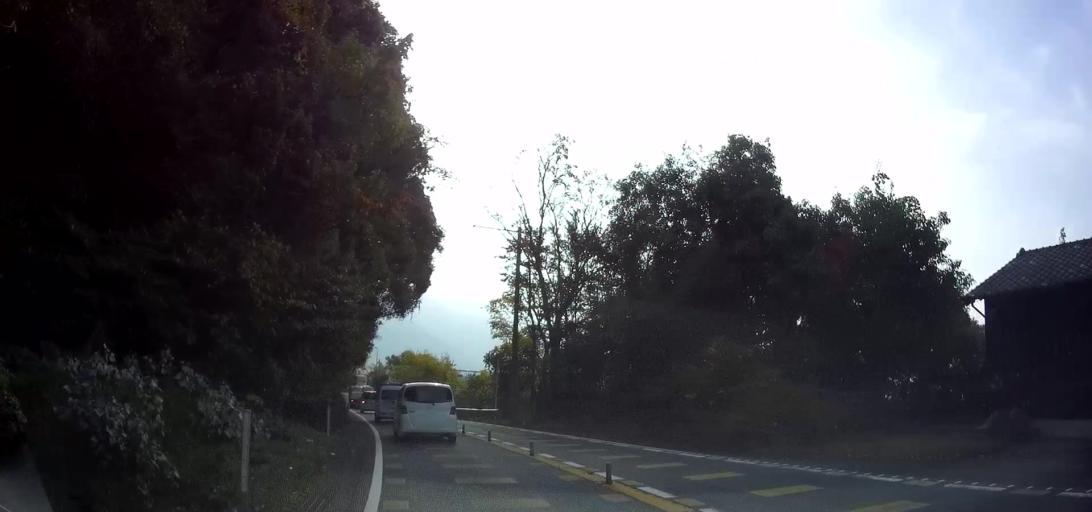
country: JP
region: Nagasaki
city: Shimabara
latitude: 32.7577
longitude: 130.2031
